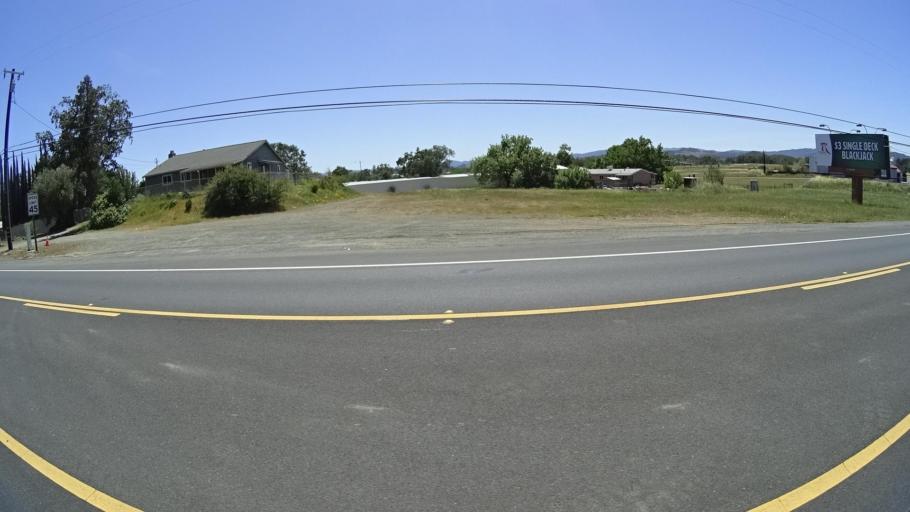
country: US
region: California
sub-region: Lake County
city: Nice
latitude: 39.1291
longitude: -122.8682
